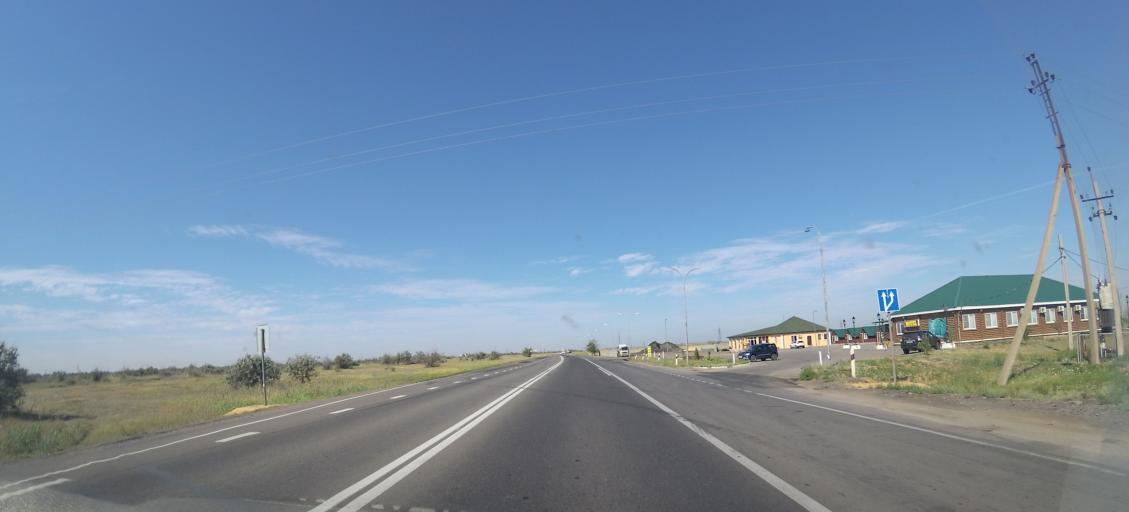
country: RU
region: Volgograd
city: Oktyabr'skiy
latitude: 48.6766
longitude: 43.8908
